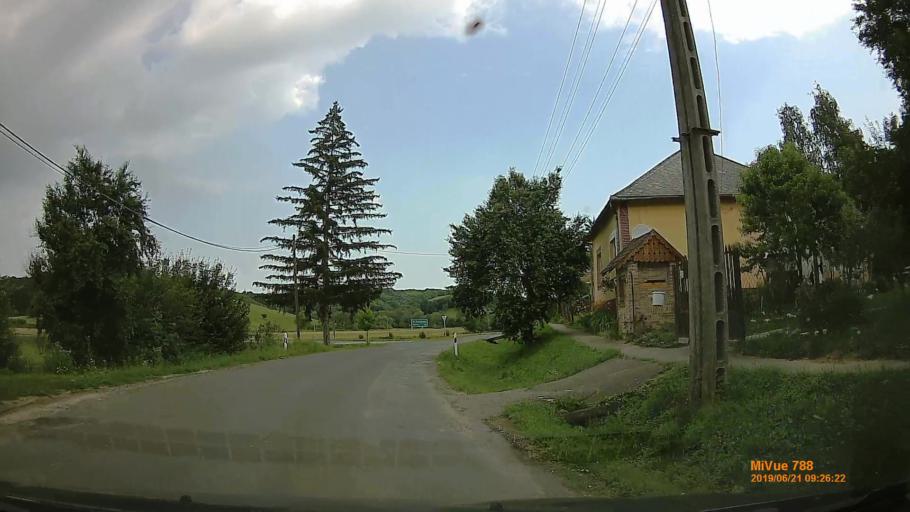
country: HU
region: Somogy
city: Taszar
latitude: 46.2727
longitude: 17.9051
